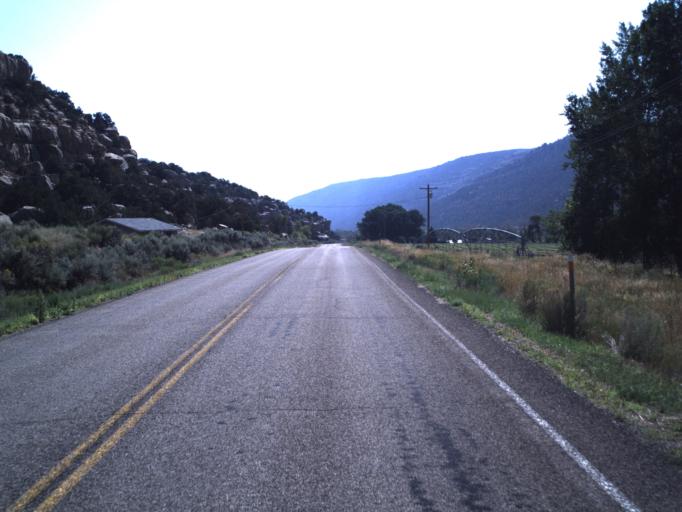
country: US
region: Utah
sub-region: Duchesne County
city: Duchesne
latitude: 40.3030
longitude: -110.6155
